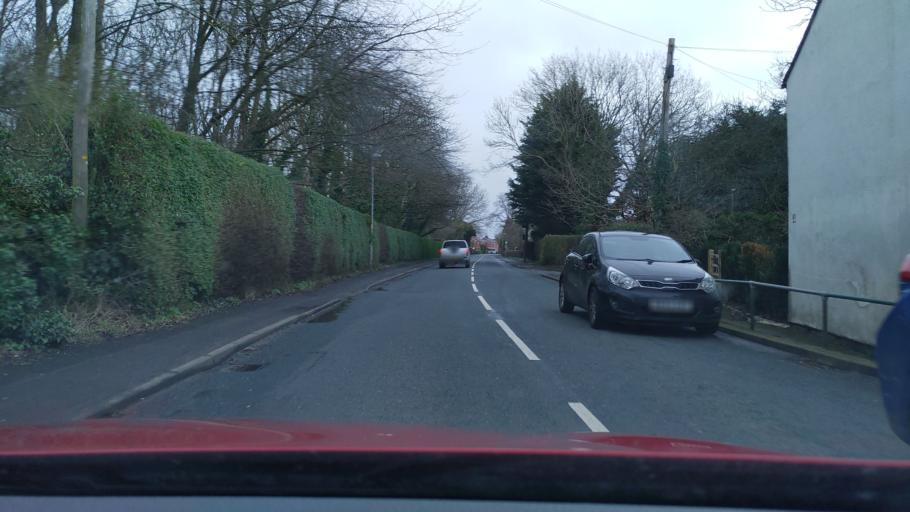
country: GB
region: England
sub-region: Lancashire
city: Croston
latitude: 53.6782
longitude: -2.7904
